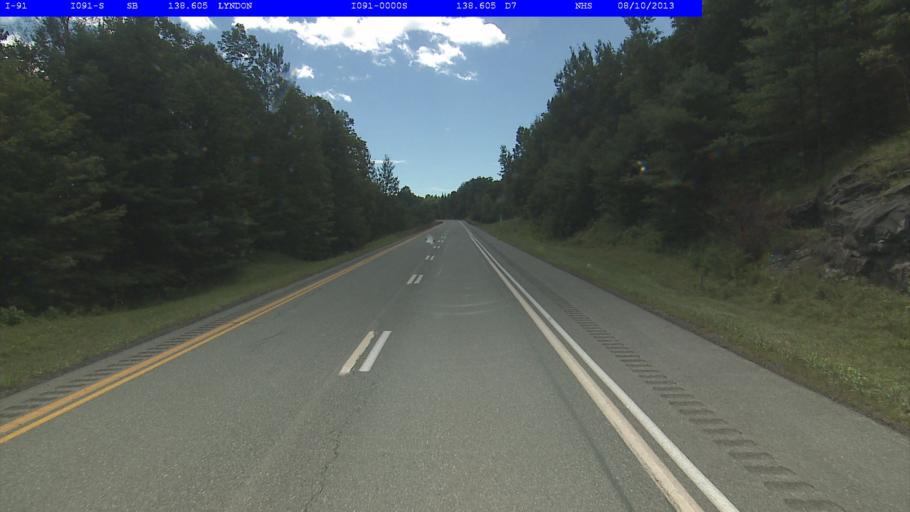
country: US
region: Vermont
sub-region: Caledonia County
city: Lyndonville
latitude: 44.5364
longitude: -72.0189
